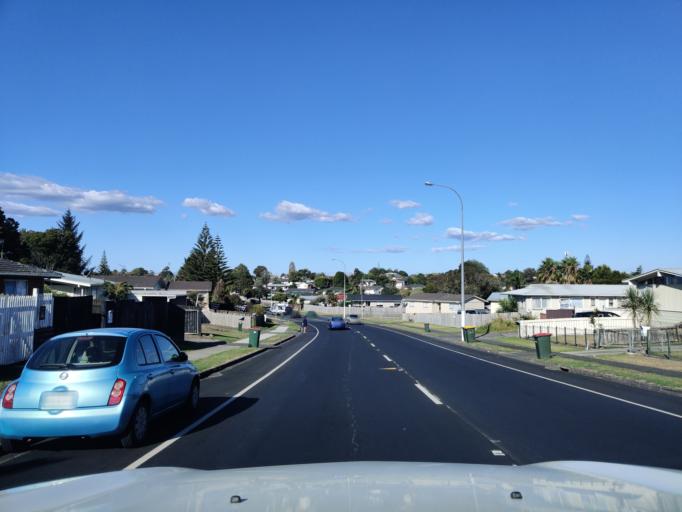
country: NZ
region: Auckland
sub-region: Auckland
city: Takanini
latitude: -37.0373
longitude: 174.8908
